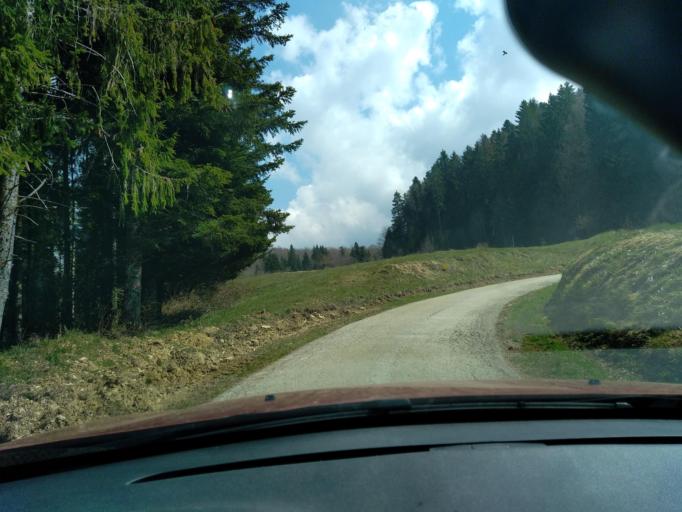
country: FR
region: Franche-Comte
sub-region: Departement du Jura
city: Lavans-les-Saint-Claude
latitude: 46.3987
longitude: 5.7514
